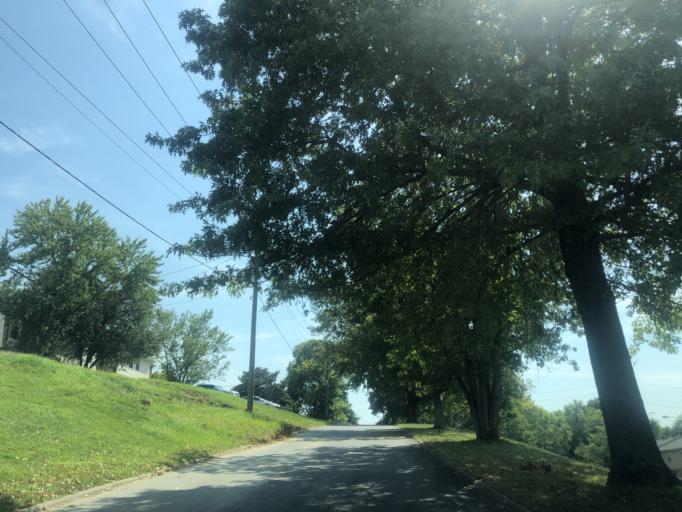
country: US
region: Tennessee
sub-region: Williamson County
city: Brentwood Estates
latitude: 36.0476
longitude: -86.7061
